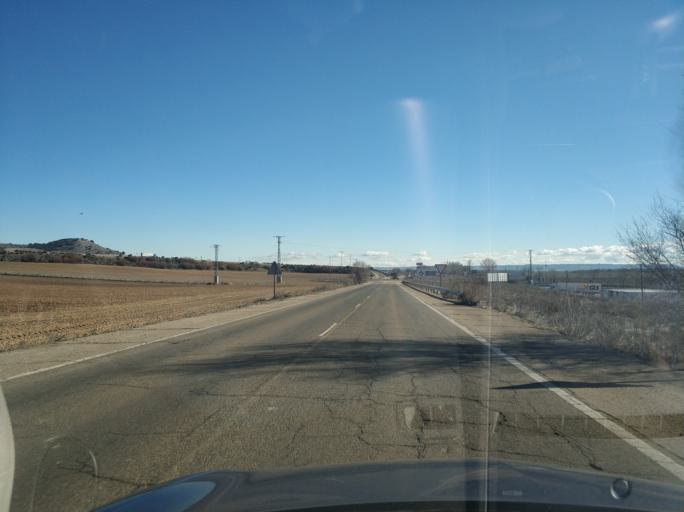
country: ES
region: Castille and Leon
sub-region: Provincia de Valladolid
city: Cisterniga
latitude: 41.6007
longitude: -4.6669
